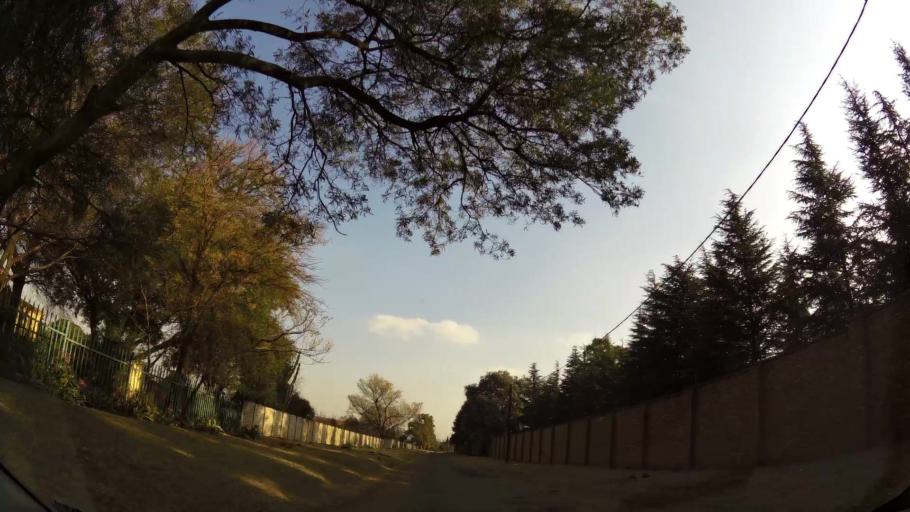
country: ZA
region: Gauteng
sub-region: Ekurhuleni Metropolitan Municipality
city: Benoni
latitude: -26.1493
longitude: 28.3724
